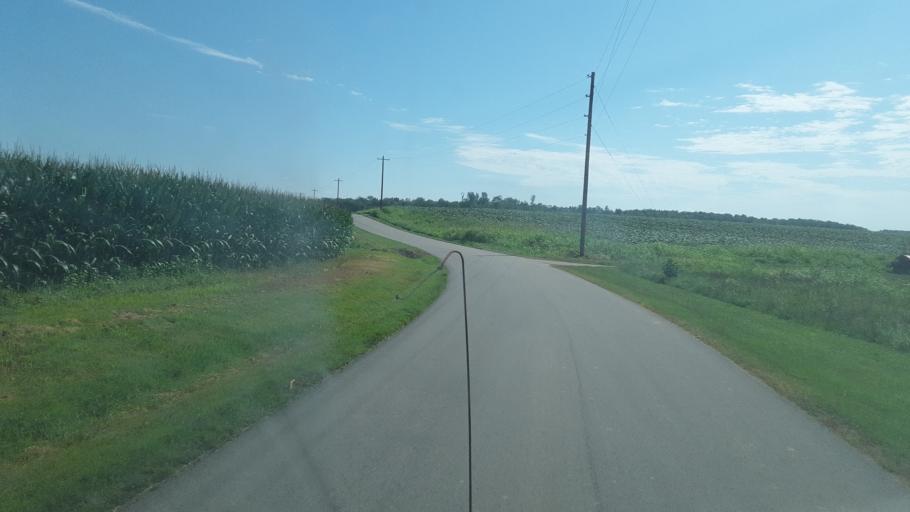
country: US
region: Kentucky
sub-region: Todd County
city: Elkton
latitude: 36.7881
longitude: -87.2113
